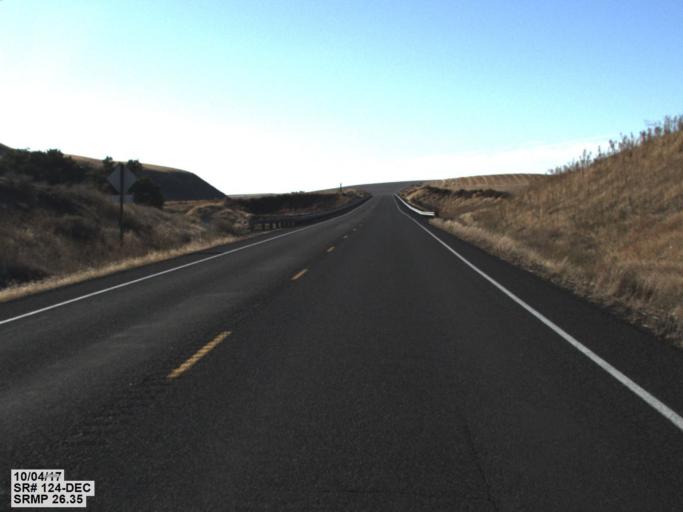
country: US
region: Washington
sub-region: Walla Walla County
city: Garrett
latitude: 46.2903
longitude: -118.5105
